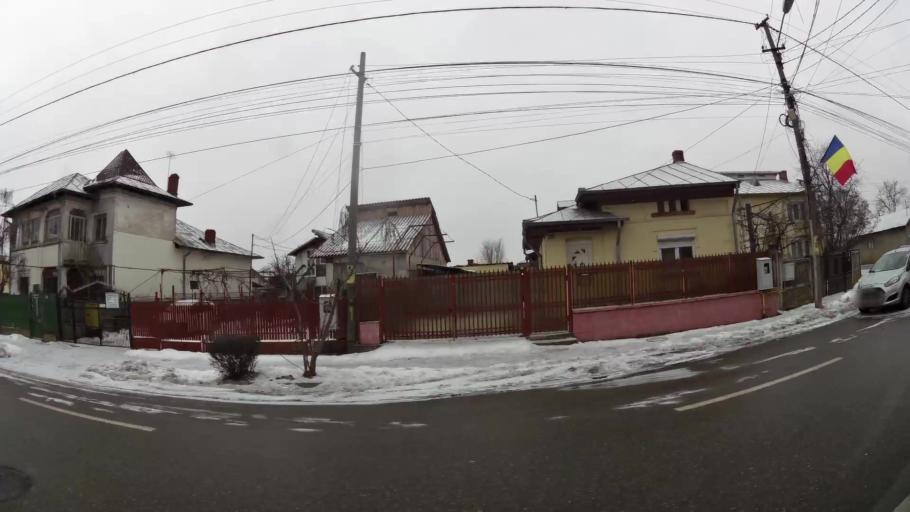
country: RO
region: Dambovita
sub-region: Municipiul Targoviste
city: Targoviste
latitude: 44.9393
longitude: 25.4453
